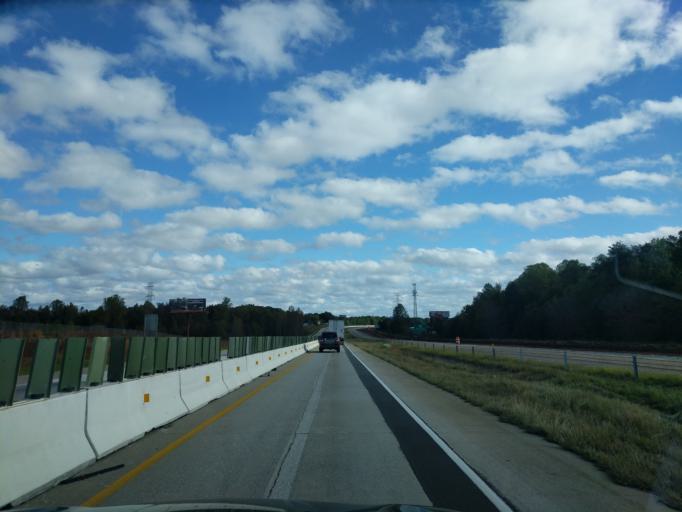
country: US
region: South Carolina
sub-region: Spartanburg County
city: Valley Falls
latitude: 35.0063
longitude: -81.9832
